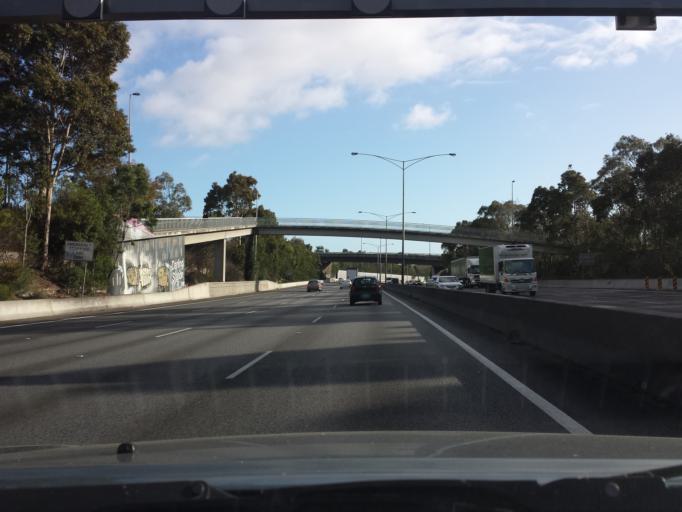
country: AU
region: Victoria
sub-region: Stonnington
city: Glen Iris
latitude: -37.8689
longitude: 145.0634
